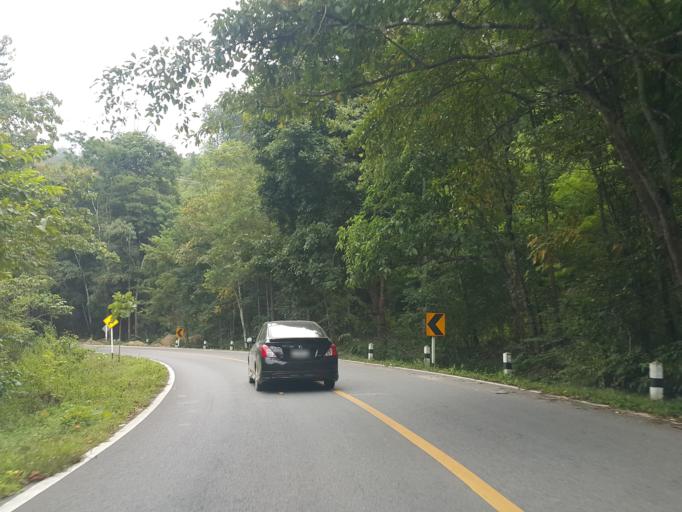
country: TH
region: Mae Hong Son
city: Mae Hi
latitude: 19.2772
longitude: 98.4967
